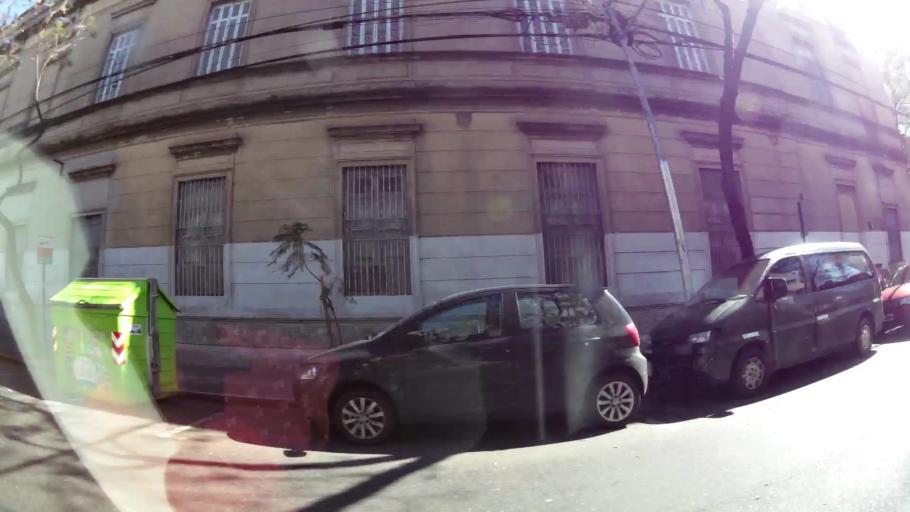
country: AR
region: Santa Fe
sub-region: Departamento de Rosario
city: Rosario
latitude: -32.9488
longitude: -60.6463
